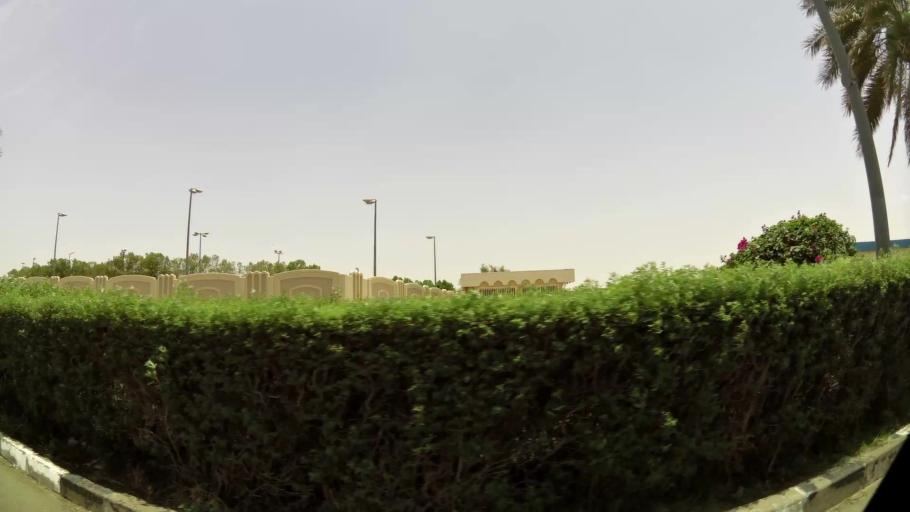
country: AE
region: Abu Dhabi
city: Al Ain
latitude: 24.2149
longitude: 55.7268
